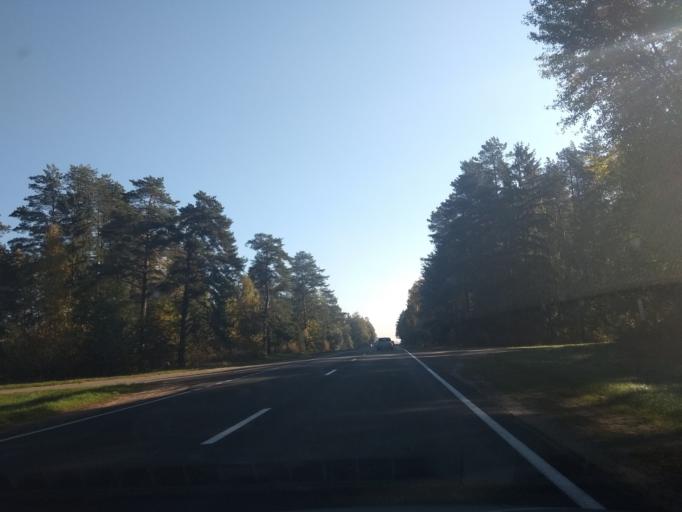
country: BY
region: Grodnenskaya
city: Zel'va
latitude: 53.1326
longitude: 25.0029
